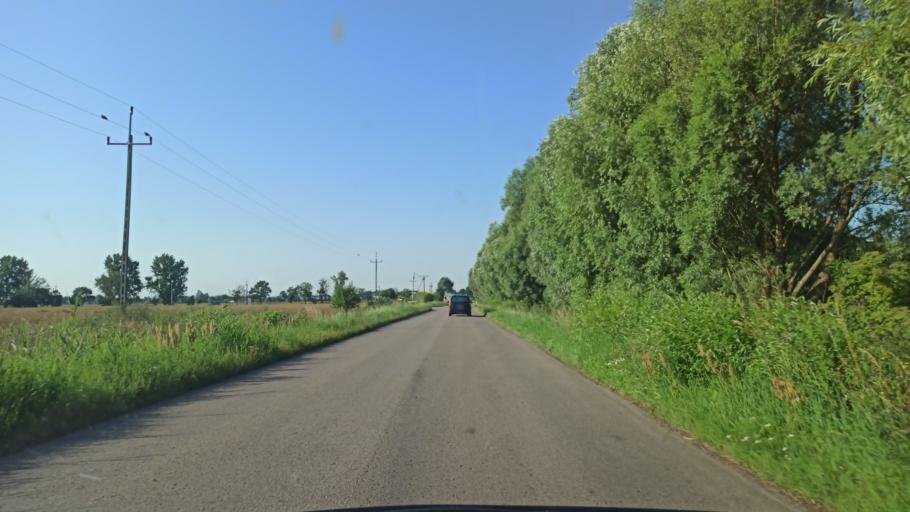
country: PL
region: Warmian-Masurian Voivodeship
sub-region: Powiat elblaski
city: Elblag
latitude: 54.1696
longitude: 19.3306
